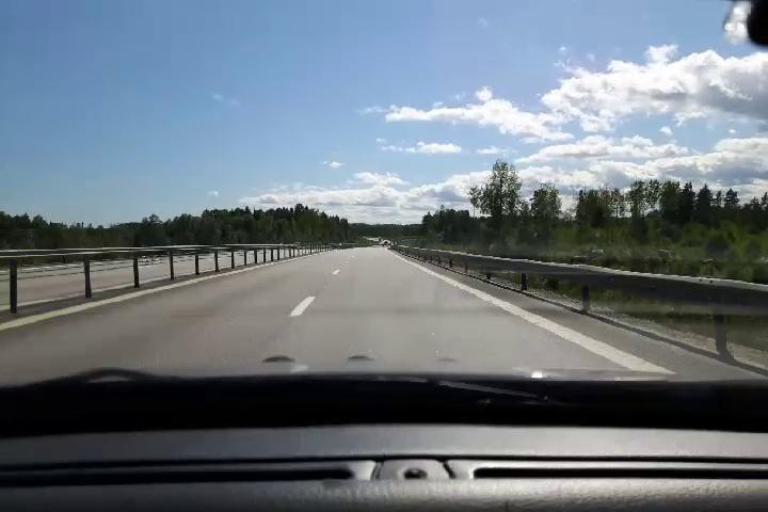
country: SE
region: Gaevleborg
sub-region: Hudiksvalls Kommun
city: Iggesund
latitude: 61.6690
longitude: 17.0285
